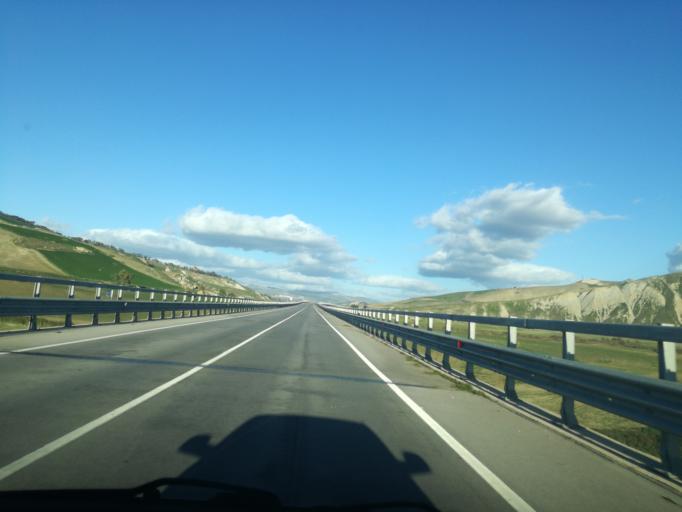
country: IT
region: Sicily
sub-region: Enna
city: Pietraperzia
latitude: 37.4274
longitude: 14.0777
